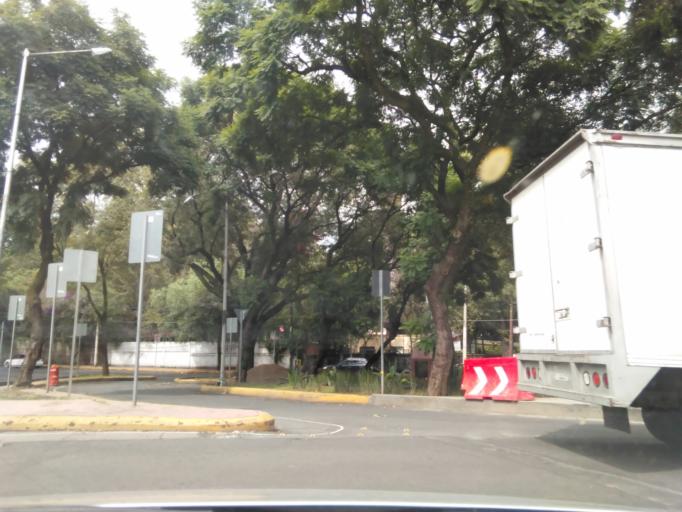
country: MX
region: Mexico City
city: Tlalpan
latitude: 19.2951
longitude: -99.1828
